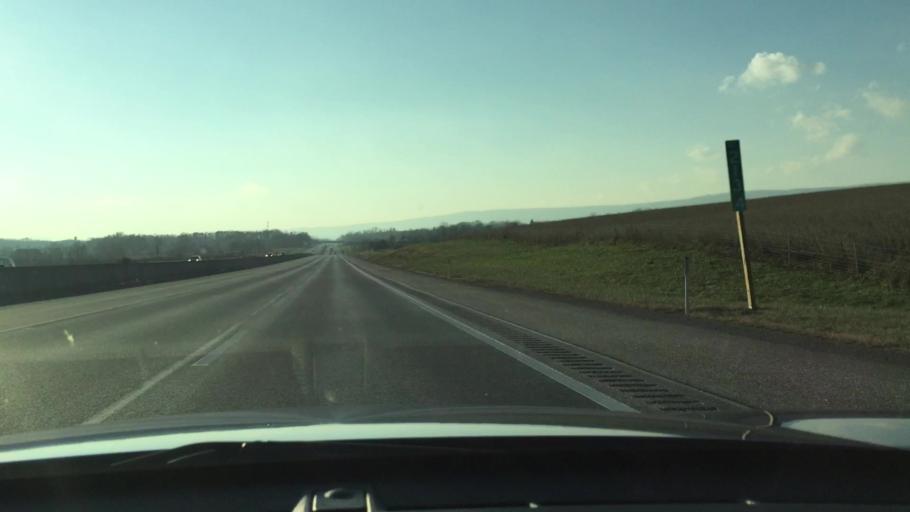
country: US
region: Pennsylvania
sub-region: Cumberland County
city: Newville
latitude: 40.1992
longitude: -77.3948
